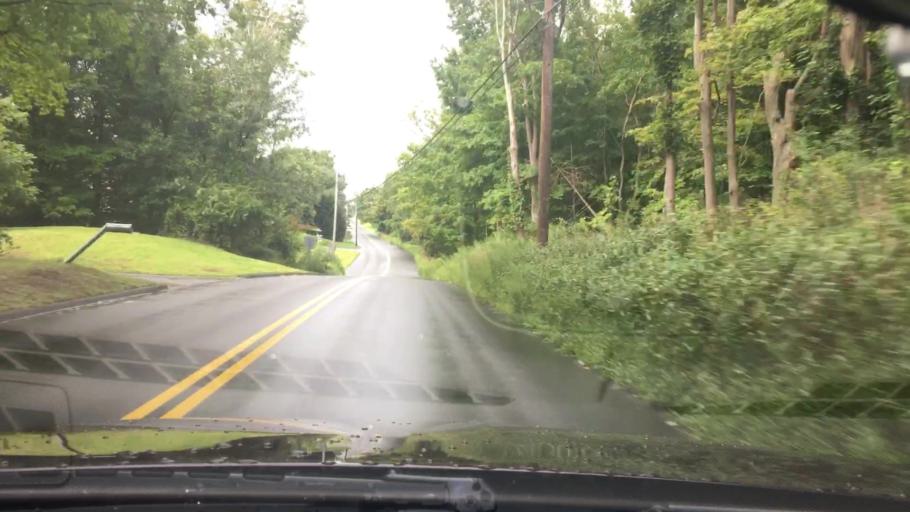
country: US
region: Connecticut
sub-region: Hartford County
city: Manchester
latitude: 41.7354
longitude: -72.5358
